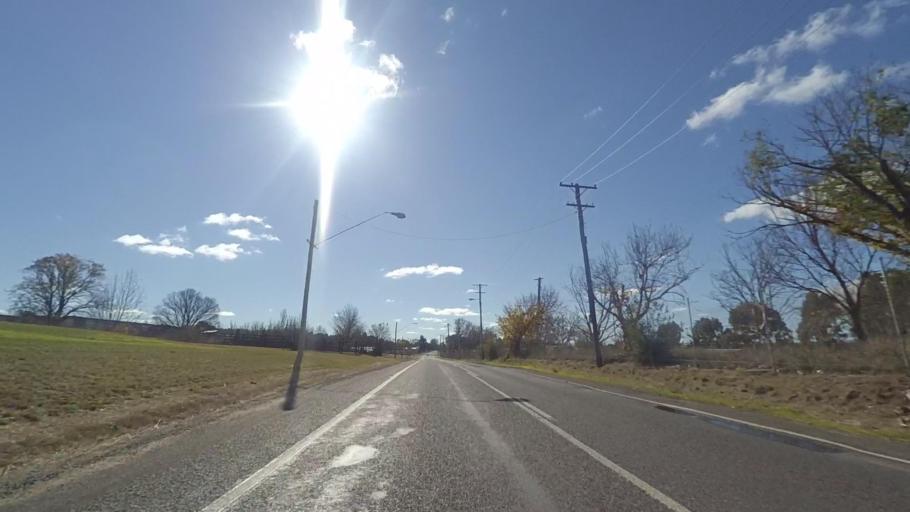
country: AU
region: New South Wales
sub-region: Bathurst Regional
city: Bathurst
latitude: -33.4426
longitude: 149.5788
